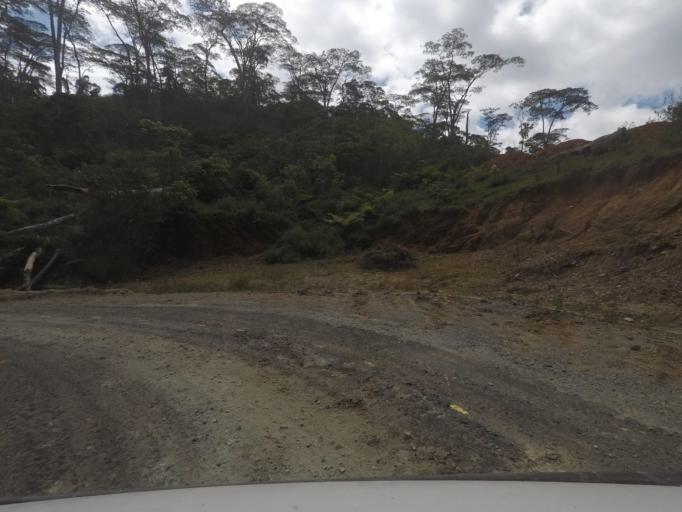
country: TL
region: Ermera
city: Gleno
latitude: -8.7471
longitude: 125.3428
